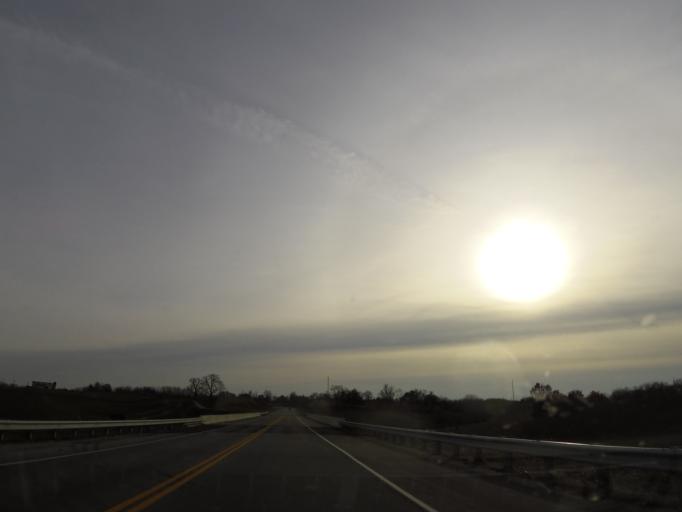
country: US
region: Kentucky
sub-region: Harrison County
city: Cynthiana
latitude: 38.3855
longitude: -84.3241
